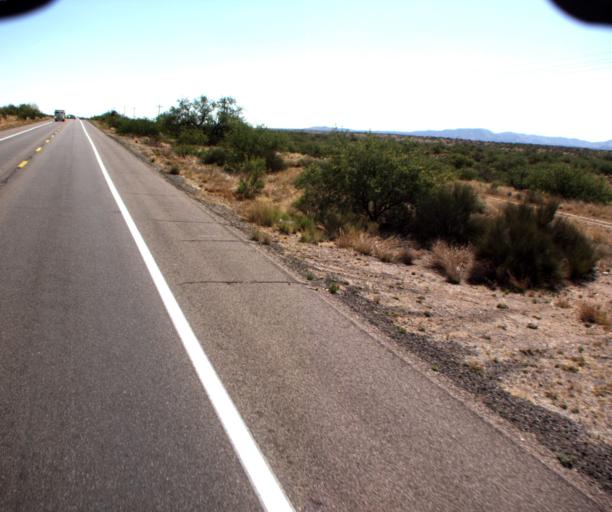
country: US
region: Arizona
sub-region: Pima County
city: Catalina
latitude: 32.5834
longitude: -110.9071
